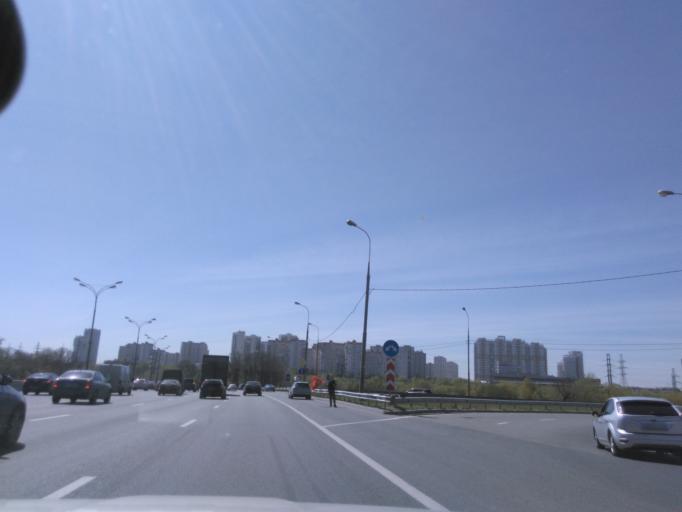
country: RU
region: Moscow
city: Strogino
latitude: 55.8498
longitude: 37.3924
